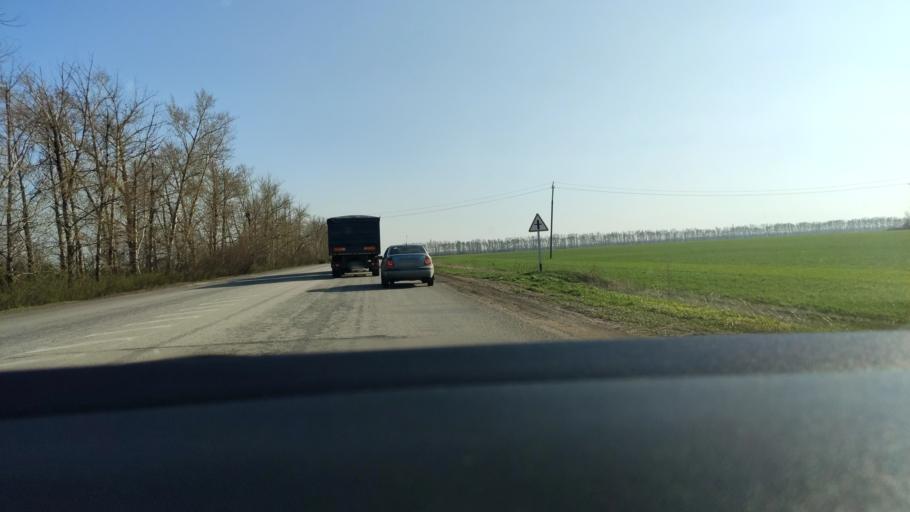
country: RU
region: Voronezj
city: Maslovka
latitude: 51.4458
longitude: 39.3027
